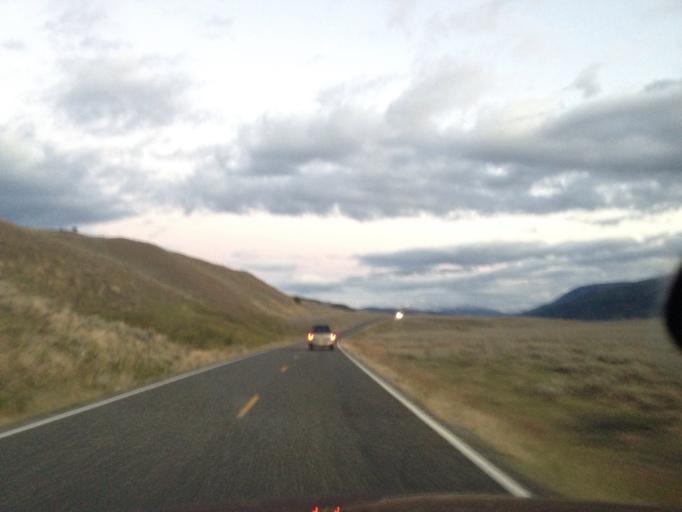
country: US
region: Montana
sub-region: Park County
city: Livingston
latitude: 44.8902
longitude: -110.2277
